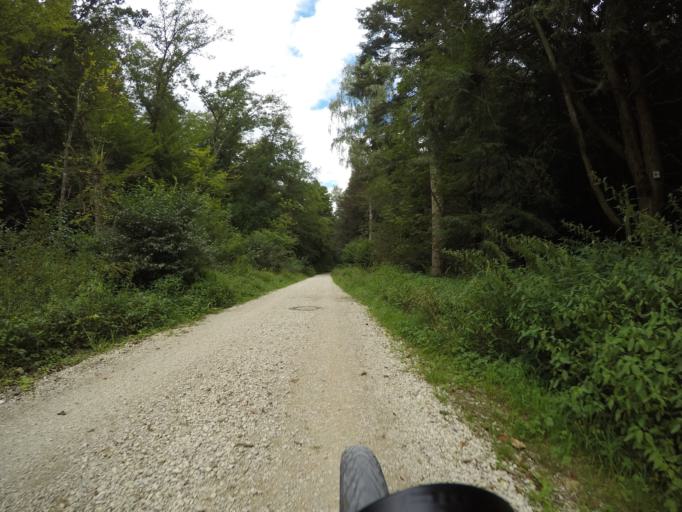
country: DE
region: Baden-Wuerttemberg
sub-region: Tuebingen Region
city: Reutlingen
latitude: 48.4580
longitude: 9.1689
